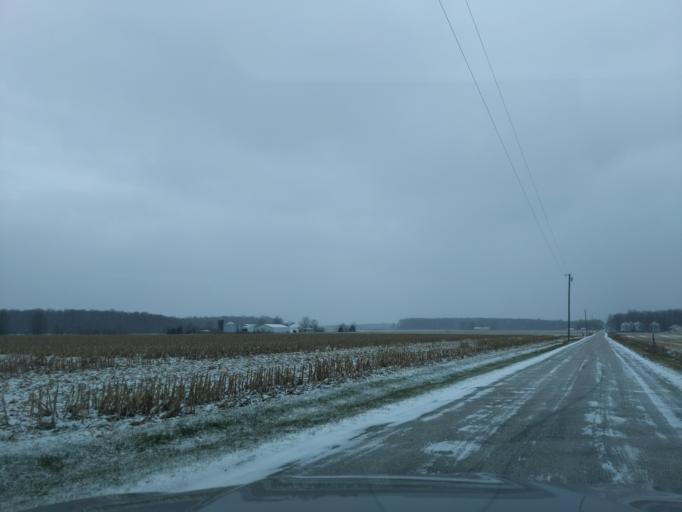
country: US
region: Indiana
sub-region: Decatur County
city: Greensburg
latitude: 39.2341
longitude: -85.4674
